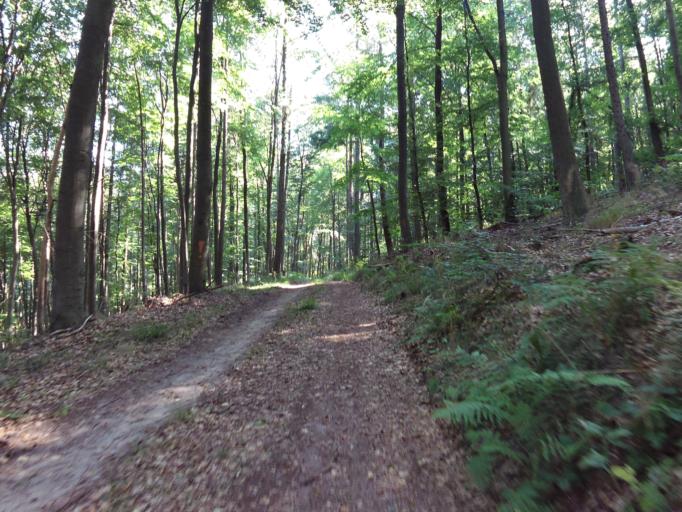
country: DE
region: Rheinland-Pfalz
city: Neidenfels
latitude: 49.4272
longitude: 8.0563
